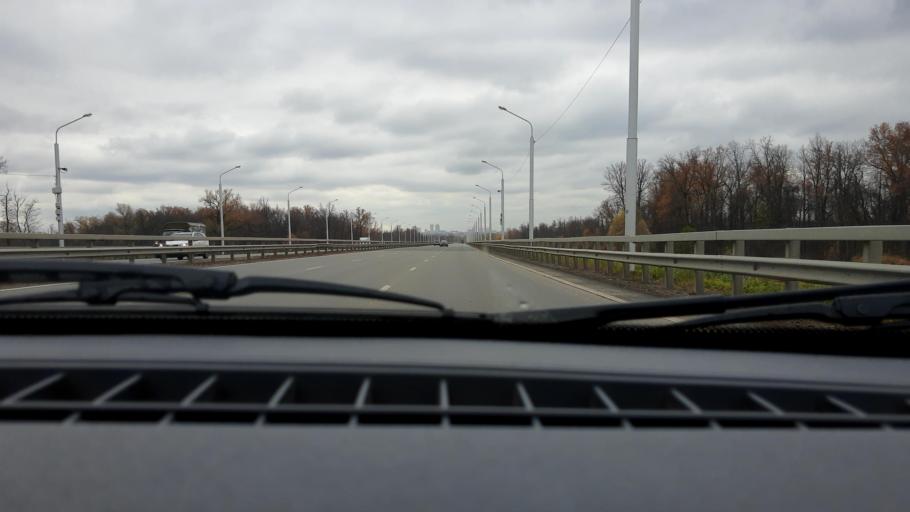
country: RU
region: Bashkortostan
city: Mikhaylovka
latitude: 54.7920
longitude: 55.9033
